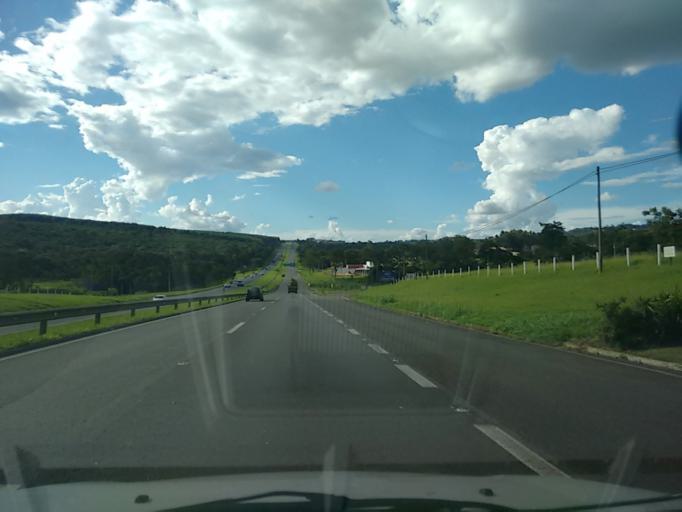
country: BR
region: Sao Paulo
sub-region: Sao Carlos
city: Sao Carlos
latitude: -22.0695
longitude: -47.8461
